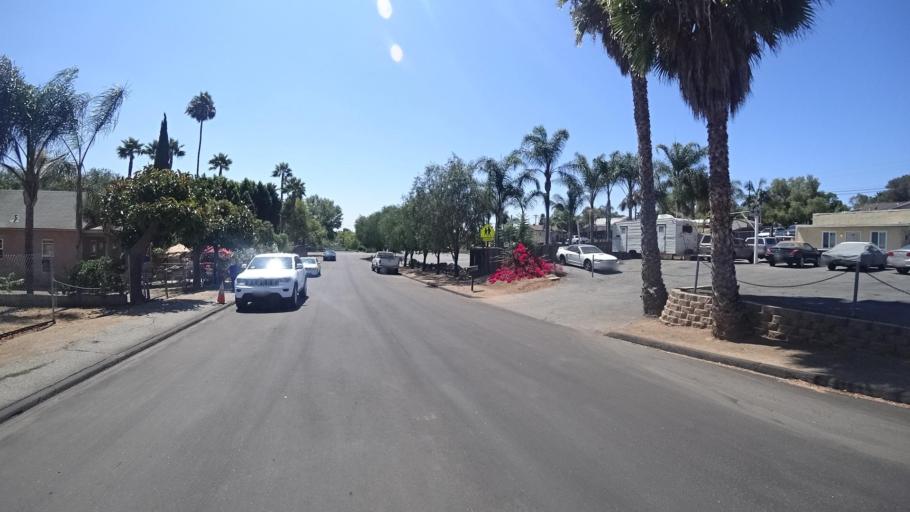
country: US
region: California
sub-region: San Diego County
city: Fallbrook
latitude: 33.3811
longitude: -117.2525
